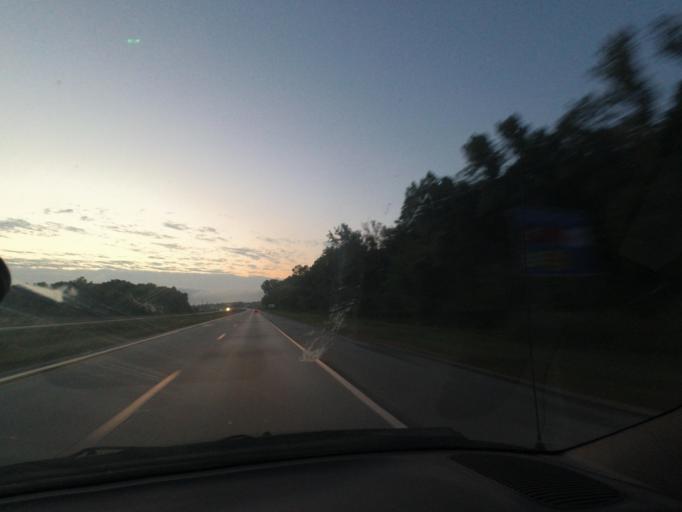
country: US
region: Missouri
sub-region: Linn County
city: Brookfield
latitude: 39.7744
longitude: -93.0859
